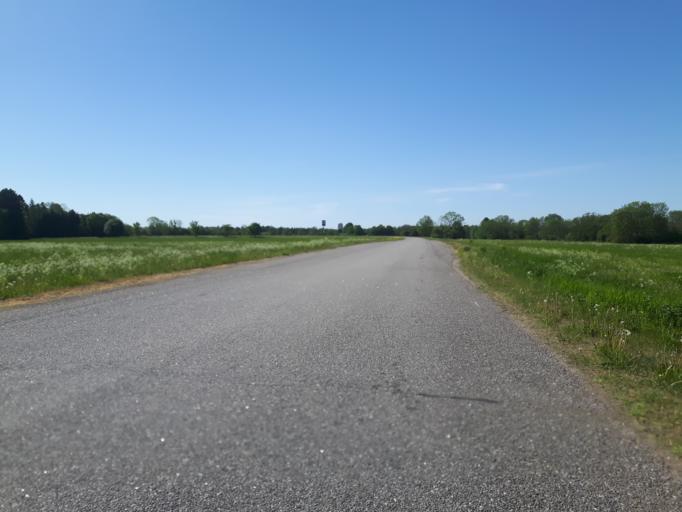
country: EE
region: Laeaene-Virumaa
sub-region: Haljala vald
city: Haljala
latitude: 59.5443
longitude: 26.2147
